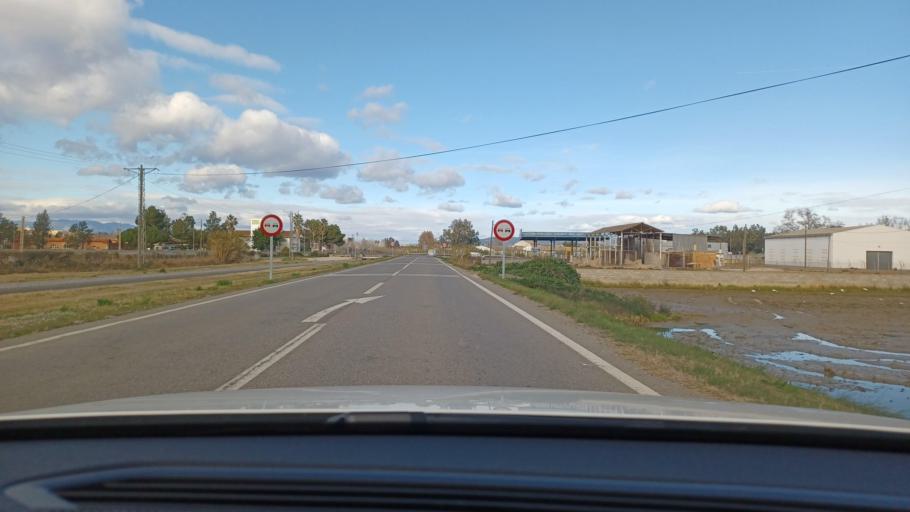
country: ES
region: Catalonia
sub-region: Provincia de Tarragona
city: Amposta
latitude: 40.7019
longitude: 0.5879
